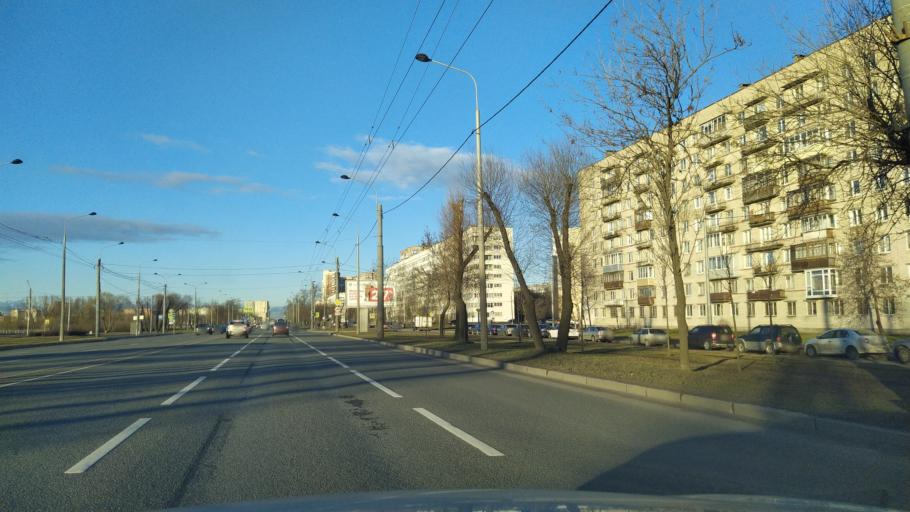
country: RU
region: St.-Petersburg
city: Uritsk
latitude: 59.8354
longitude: 30.1979
